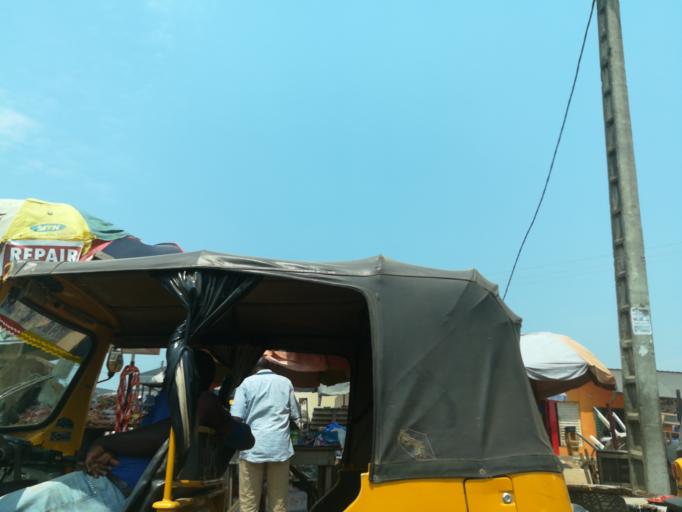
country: NG
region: Lagos
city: Ikorodu
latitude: 6.6276
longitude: 3.4837
